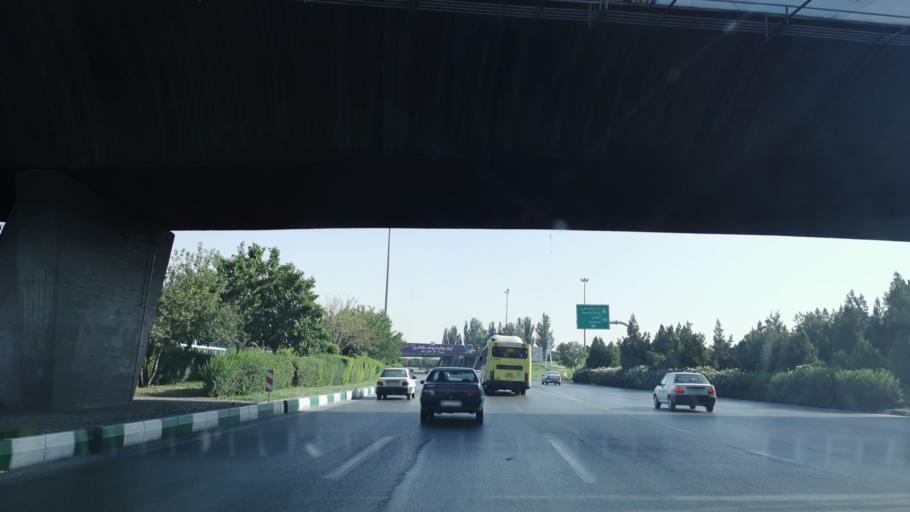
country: IR
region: Razavi Khorasan
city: Mashhad
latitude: 36.3429
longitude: 59.5480
